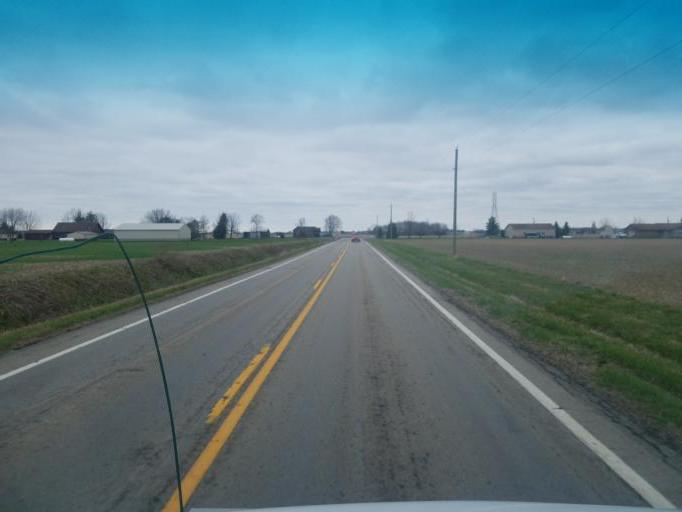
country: US
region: Ohio
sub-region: Allen County
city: Delphos
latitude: 40.9159
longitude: -84.3507
